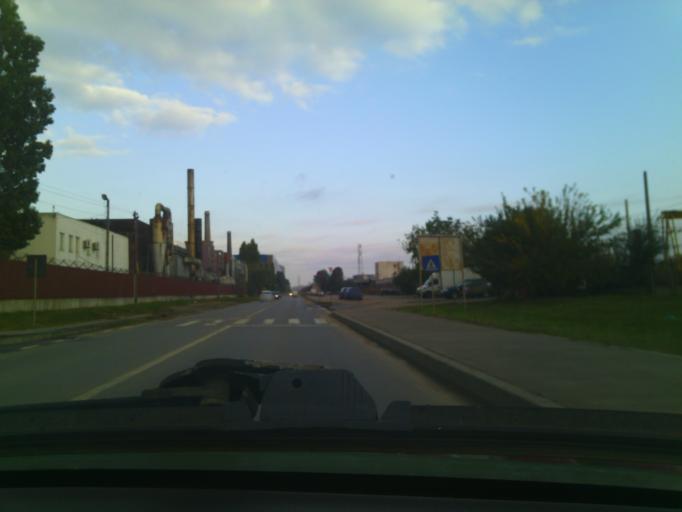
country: RO
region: Ilfov
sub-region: Comuna Popesti-Leordeni
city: Popesti-Leordeni
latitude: 44.3582
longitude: 26.1513
